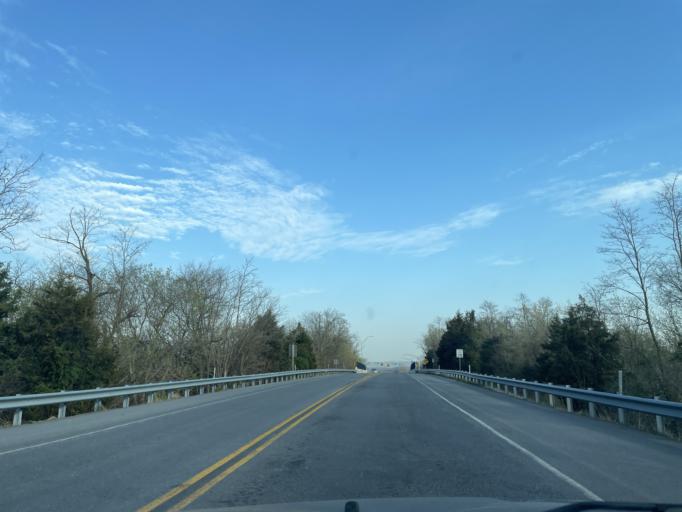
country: US
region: Maryland
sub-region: Washington County
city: Williamsport
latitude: 39.5834
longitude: -77.8115
